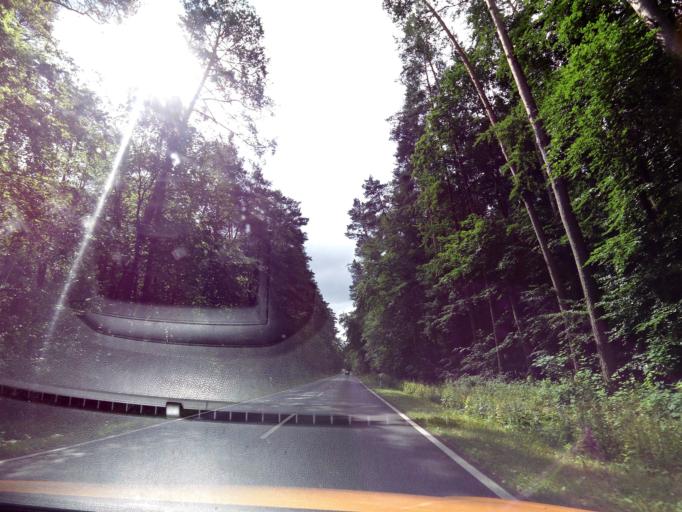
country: DE
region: Mecklenburg-Vorpommern
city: Muhl Rosin
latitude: 53.7498
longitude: 12.2548
